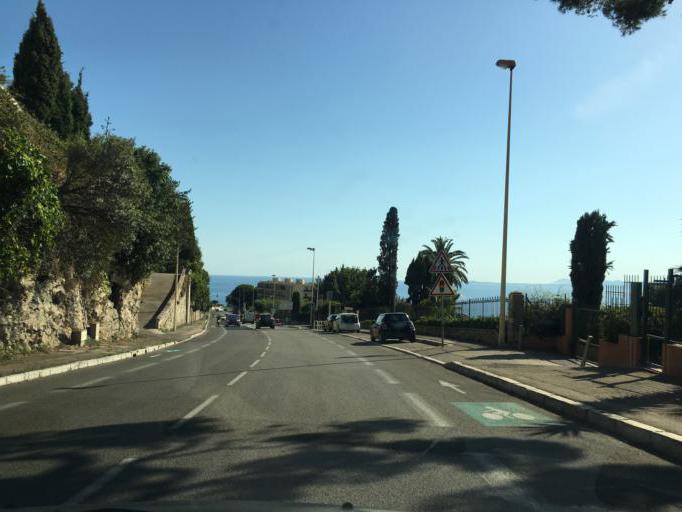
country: FR
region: Provence-Alpes-Cote d'Azur
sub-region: Departement des Alpes-Maritimes
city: Villefranche-sur-Mer
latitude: 43.7006
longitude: 7.2965
